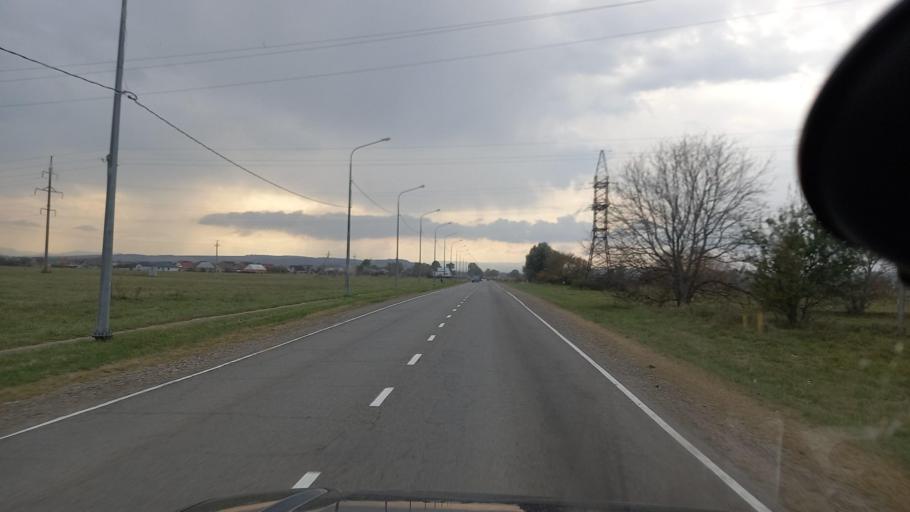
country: RU
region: Krasnodarskiy
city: Mostovskoy
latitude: 44.4011
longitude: 40.7795
